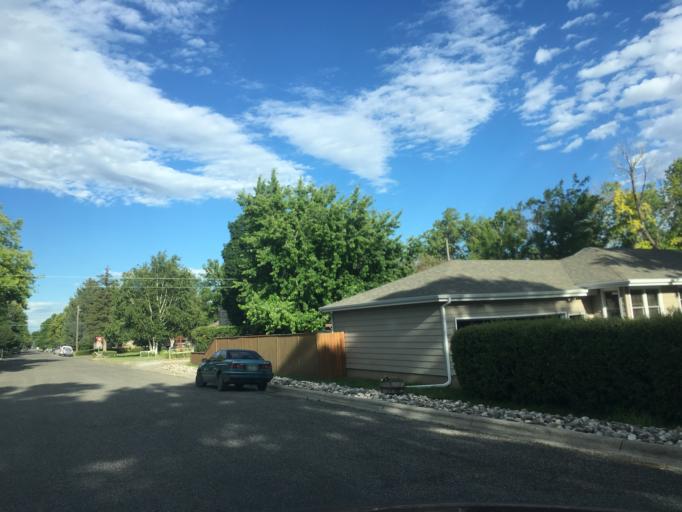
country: US
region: Montana
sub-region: Yellowstone County
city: Billings
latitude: 45.7970
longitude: -108.5741
